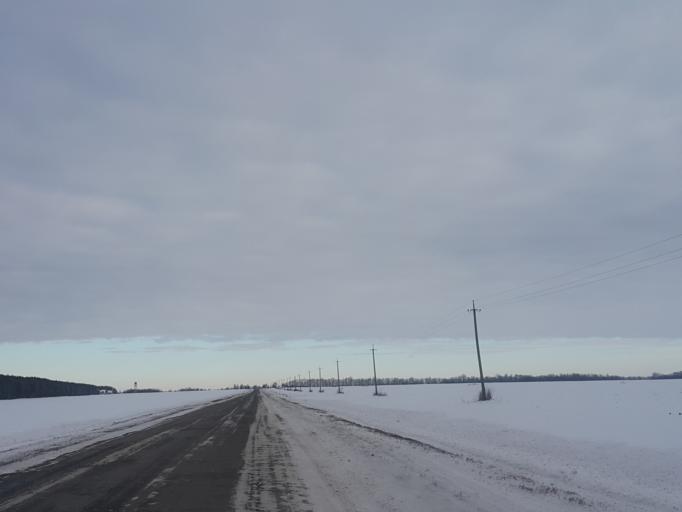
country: RU
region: Tambov
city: Novaya Lyada
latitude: 52.7568
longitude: 41.7241
